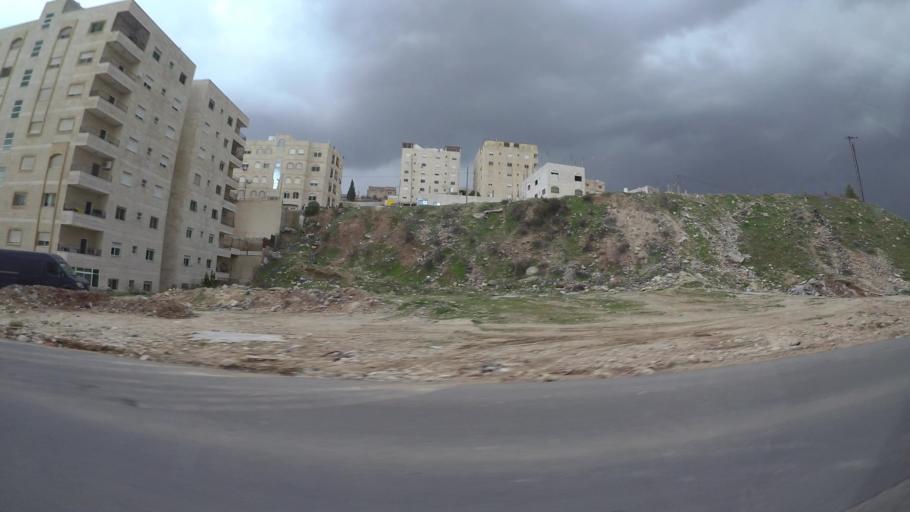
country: JO
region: Amman
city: Amman
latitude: 32.0113
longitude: 35.9473
